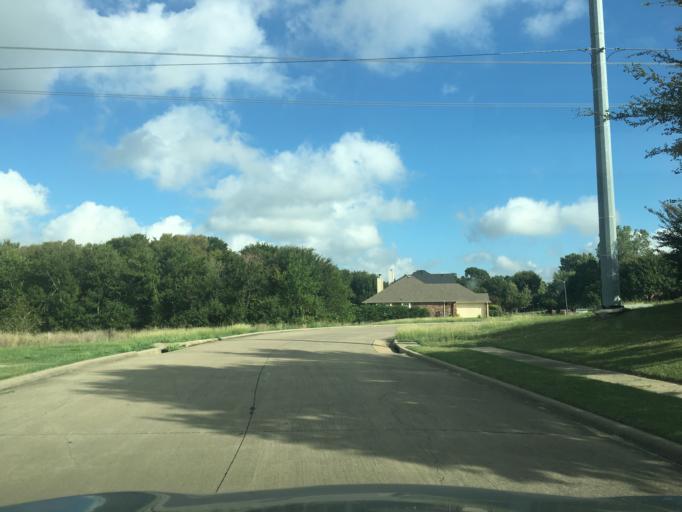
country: US
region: Texas
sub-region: Dallas County
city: Sachse
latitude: 32.9639
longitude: -96.5933
